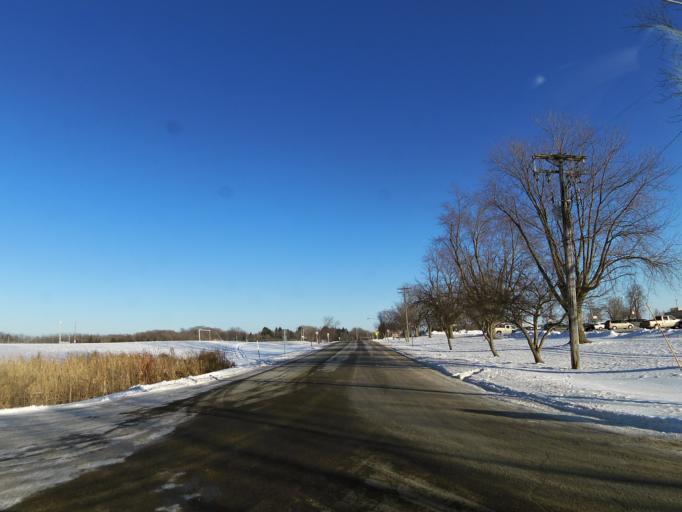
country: US
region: Minnesota
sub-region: Hennepin County
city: Mound
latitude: 44.9567
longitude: -93.6731
